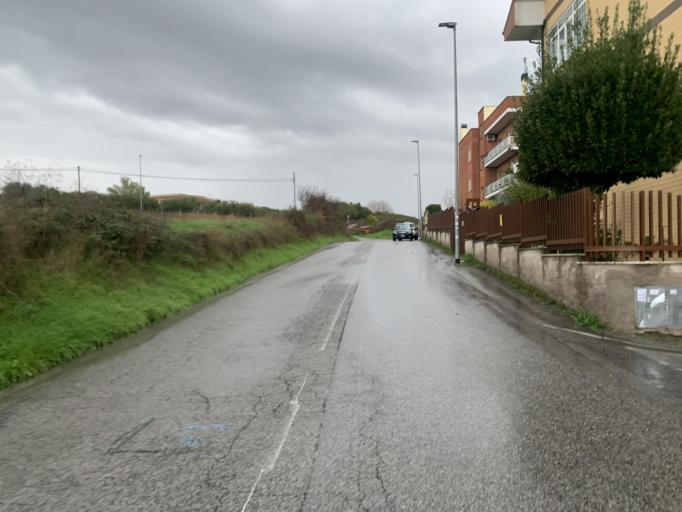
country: IT
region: Latium
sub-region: Citta metropolitana di Roma Capitale
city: Setteville
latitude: 41.9454
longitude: 12.6529
